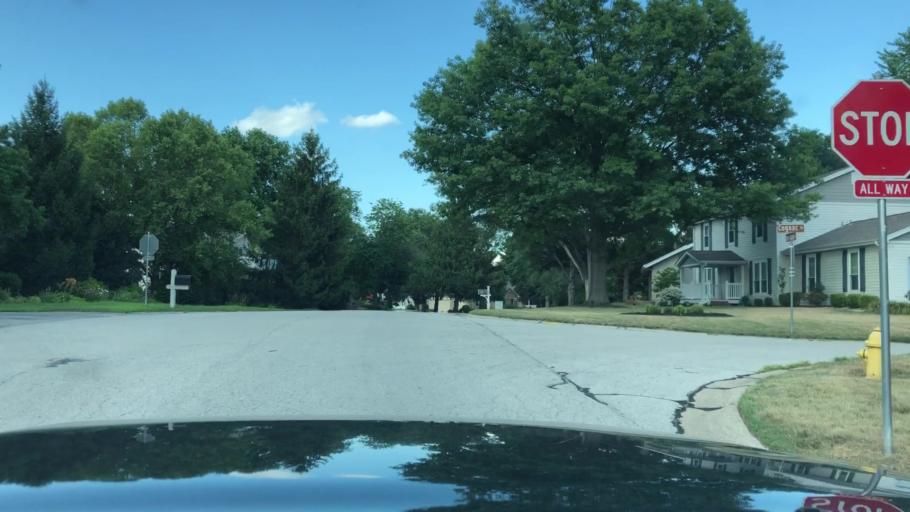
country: US
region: Missouri
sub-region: Saint Charles County
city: Lake Saint Louis
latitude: 38.7960
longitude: -90.7938
